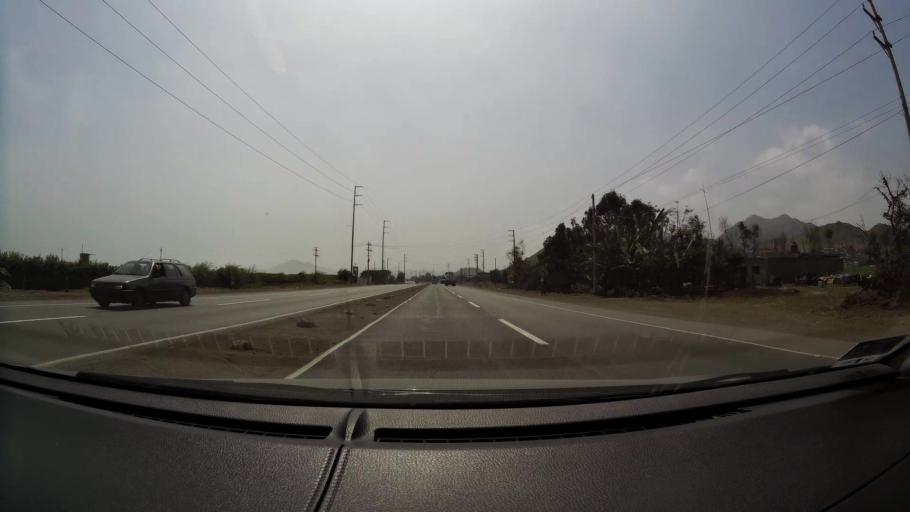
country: PE
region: Lima
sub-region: Provincia de Huaral
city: Chancay
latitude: -11.5279
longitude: -77.2882
